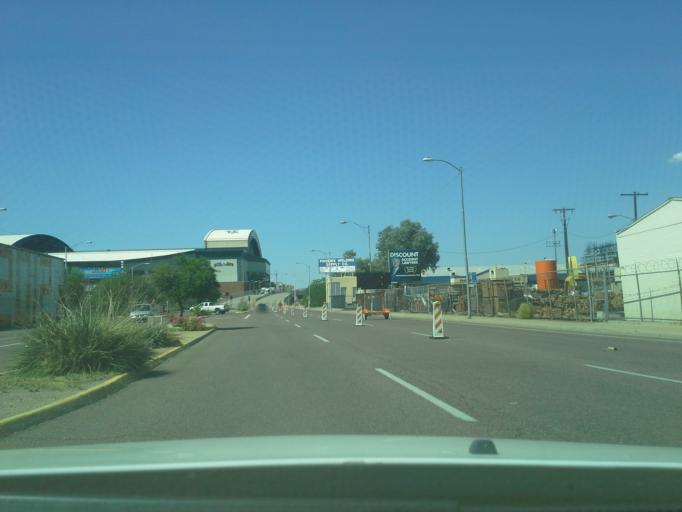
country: US
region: Arizona
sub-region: Maricopa County
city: Phoenix
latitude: 33.4400
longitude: -112.0651
